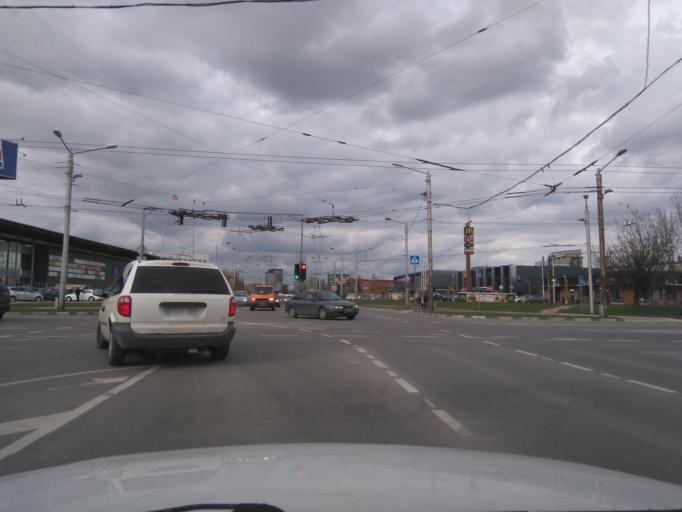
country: LT
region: Kauno apskritis
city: Dainava (Kaunas)
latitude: 54.9106
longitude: 23.9835
